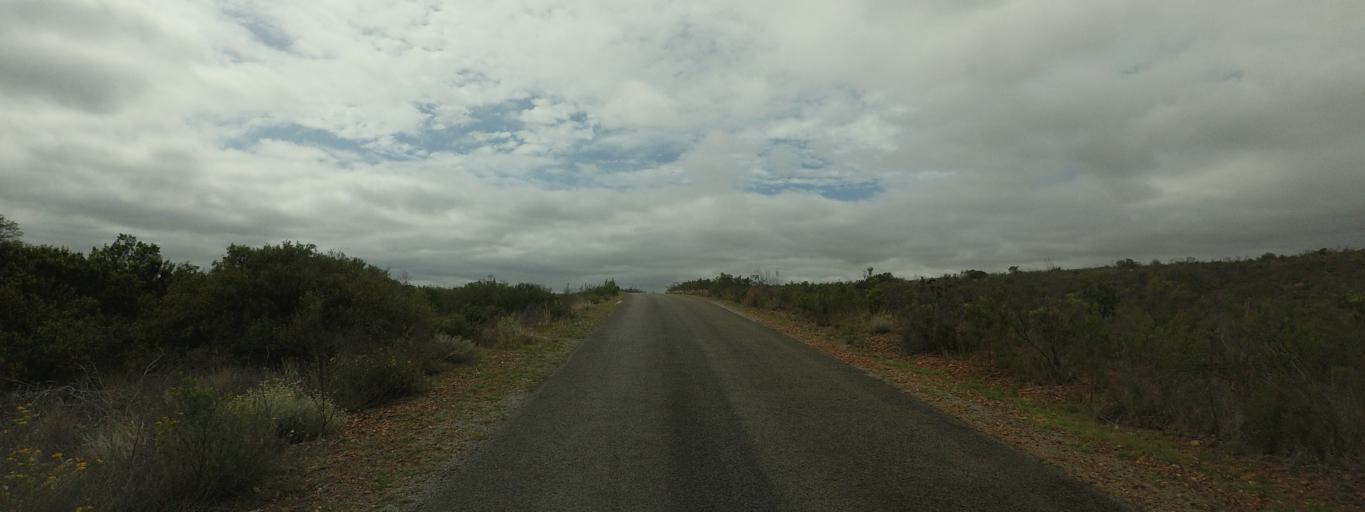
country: ZA
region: Western Cape
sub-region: Overberg District Municipality
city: Swellendam
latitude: -34.0547
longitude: 20.4301
